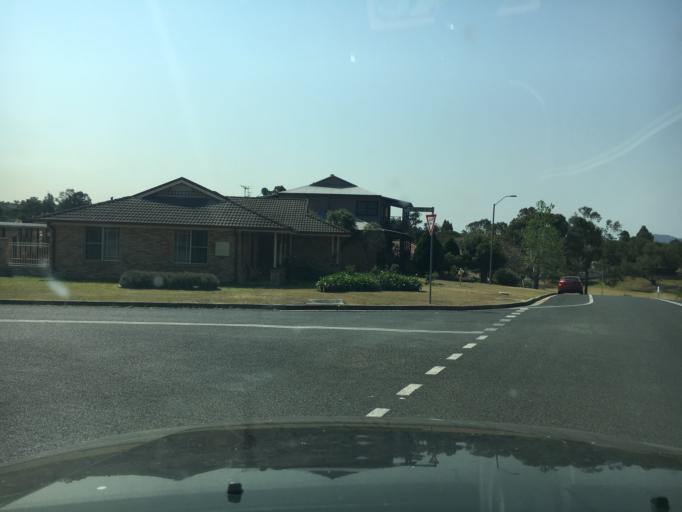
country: AU
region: New South Wales
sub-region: Singleton
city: Singleton
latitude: -32.5603
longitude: 151.1594
